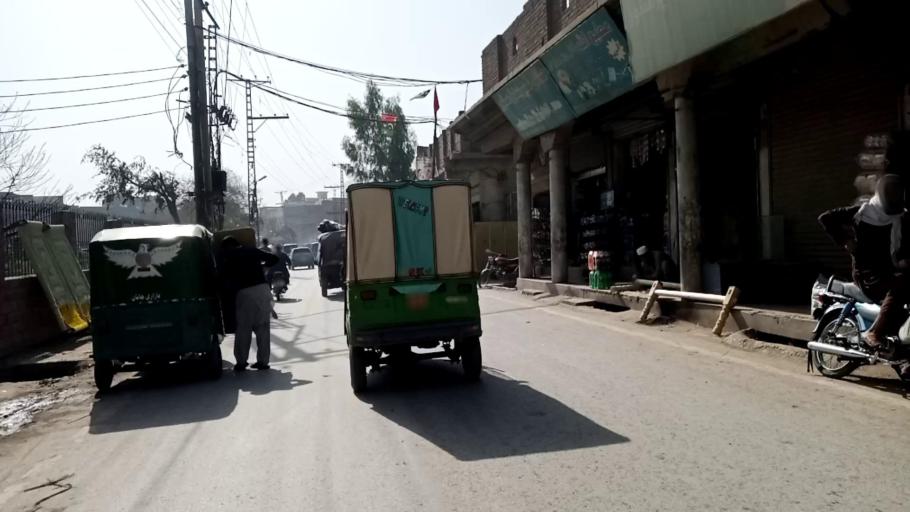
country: PK
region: Khyber Pakhtunkhwa
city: Peshawar
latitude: 34.0039
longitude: 71.5849
